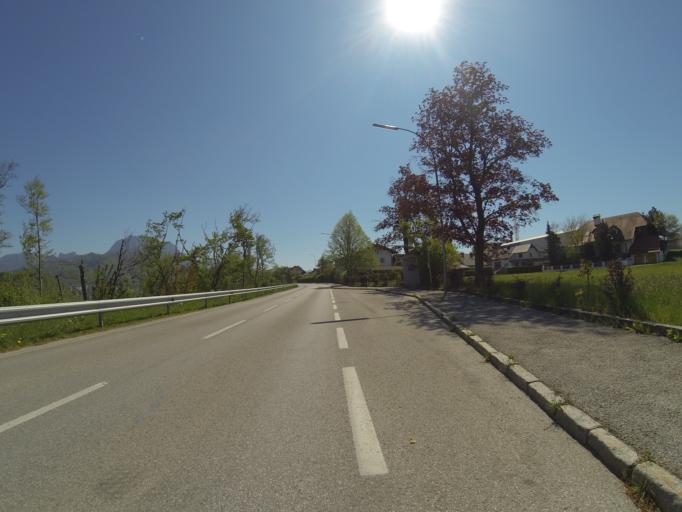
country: AT
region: Upper Austria
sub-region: Politischer Bezirk Gmunden
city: Gmunden
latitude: 47.9333
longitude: 13.7943
